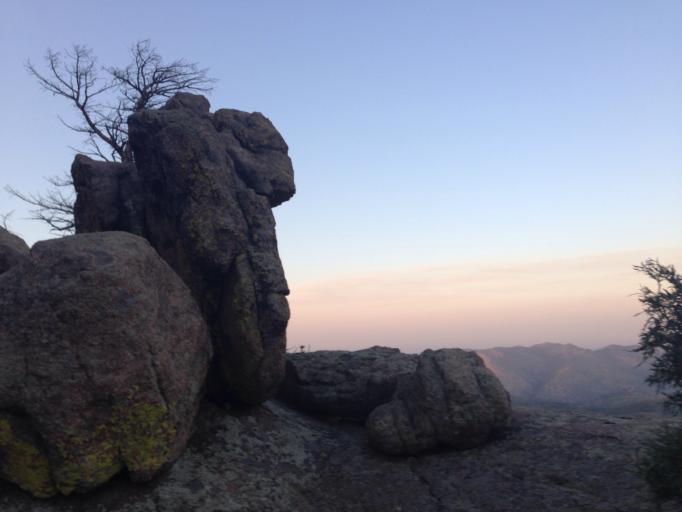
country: US
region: Colorado
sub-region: Larimer County
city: Laporte
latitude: 40.7173
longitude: -105.2886
